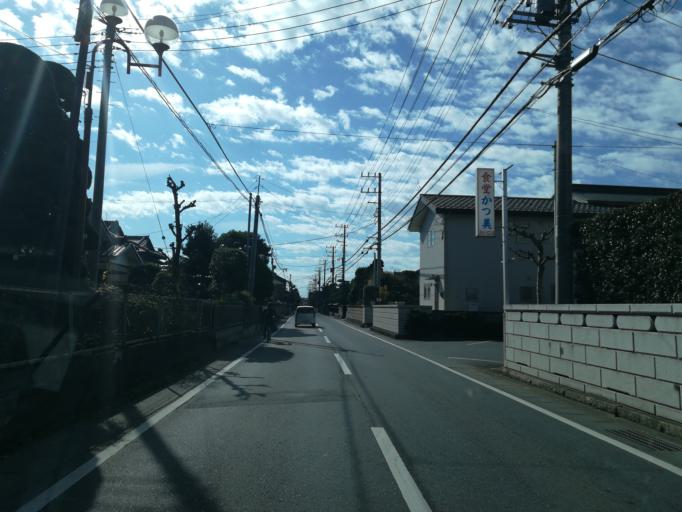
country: JP
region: Ibaraki
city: Naka
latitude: 36.0808
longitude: 140.1009
